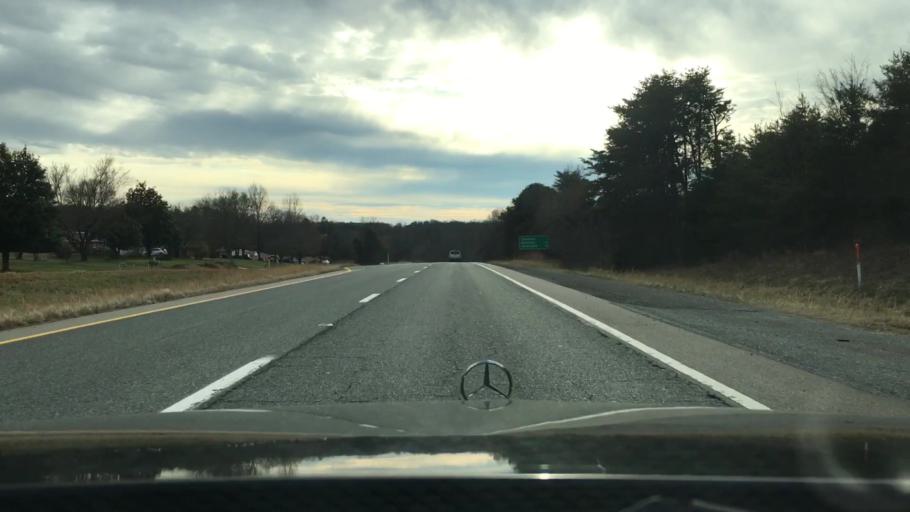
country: US
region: Virginia
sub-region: Pittsylvania County
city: Gretna
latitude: 36.9179
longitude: -79.3847
